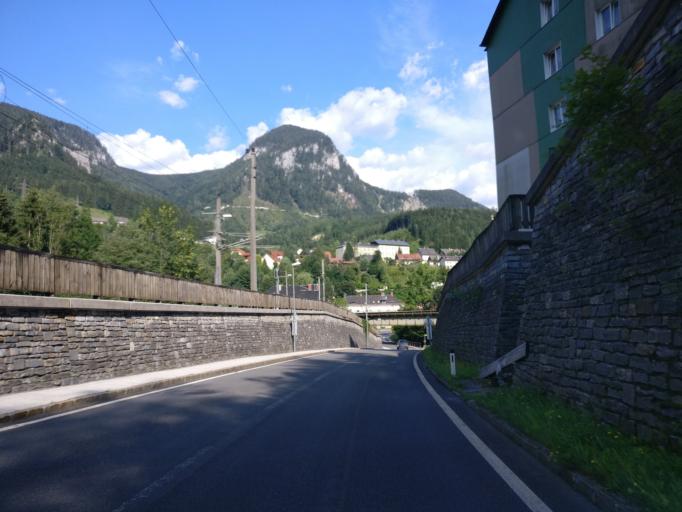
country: AT
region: Styria
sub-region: Politischer Bezirk Leoben
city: Hieflau
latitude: 47.6080
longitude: 14.7411
